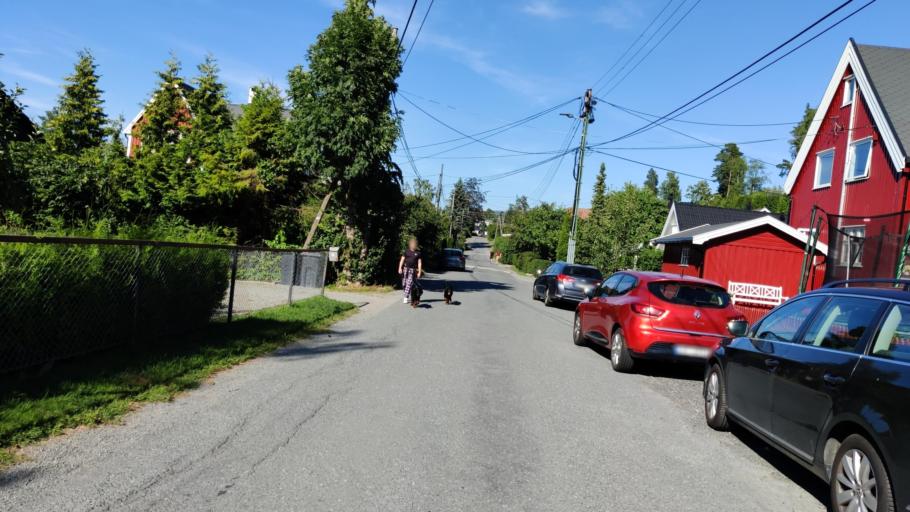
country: NO
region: Akershus
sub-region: Baerum
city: Lysaker
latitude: 59.9220
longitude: 10.5939
